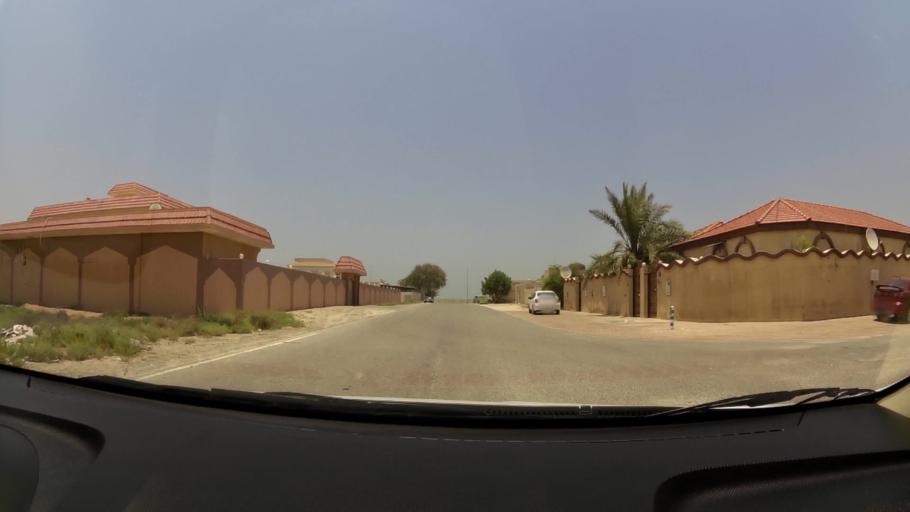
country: AE
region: Umm al Qaywayn
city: Umm al Qaywayn
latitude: 25.5347
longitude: 55.5346
